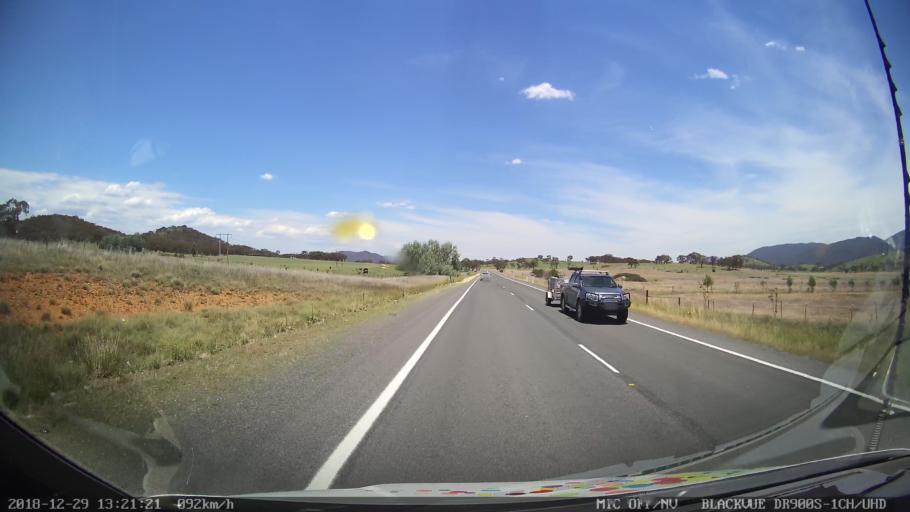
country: AU
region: Australian Capital Territory
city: Macarthur
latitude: -35.7910
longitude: 149.1638
